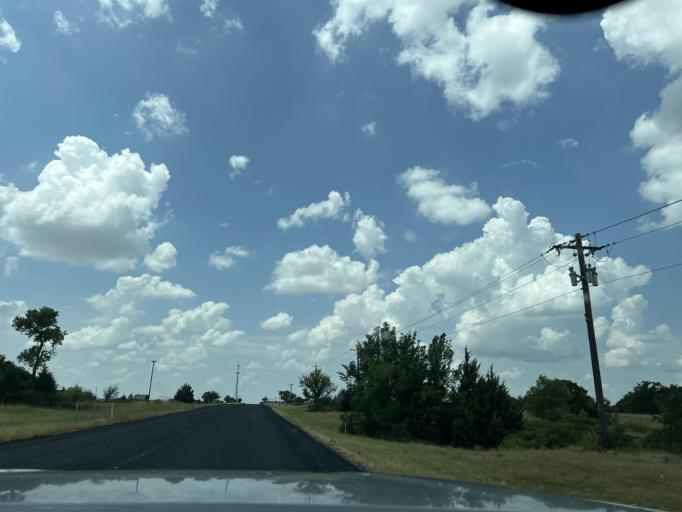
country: US
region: Texas
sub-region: Wise County
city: Boyd
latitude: 33.0728
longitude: -97.6503
